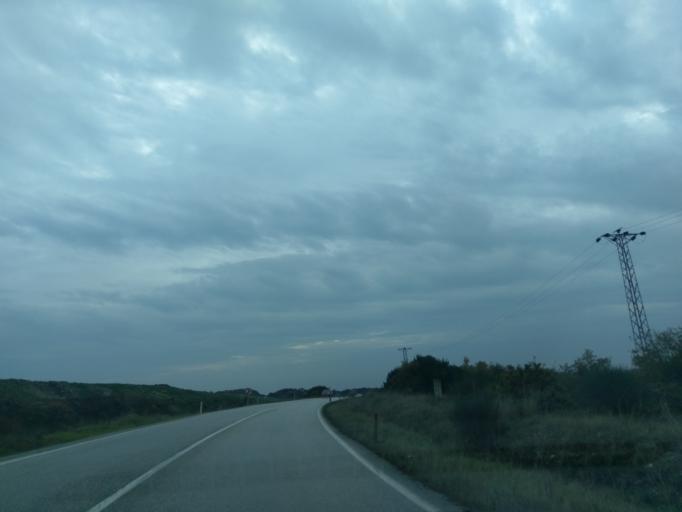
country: TR
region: Istanbul
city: Canta
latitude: 41.1607
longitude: 28.1062
